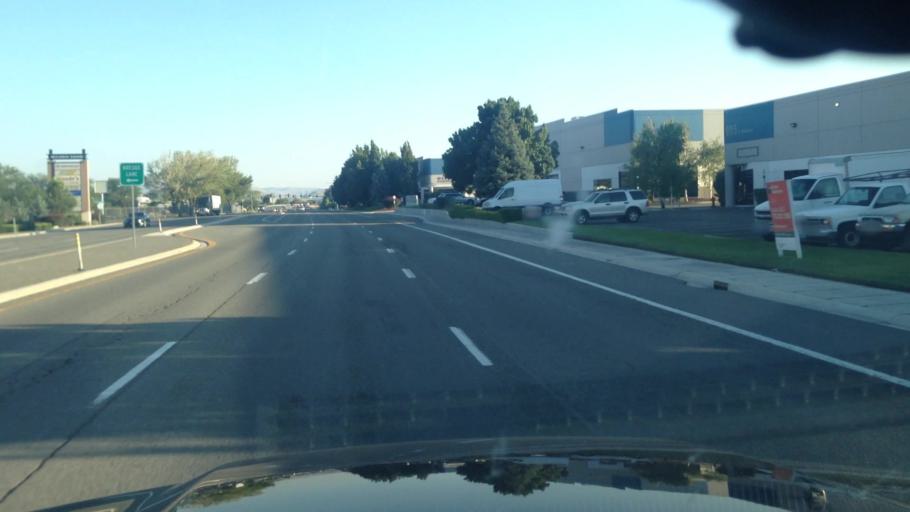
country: US
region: Nevada
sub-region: Washoe County
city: Sparks
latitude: 39.5253
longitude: -119.7398
